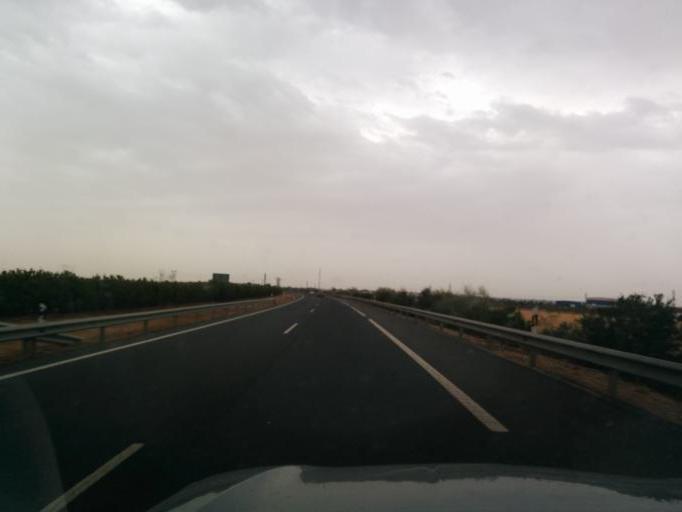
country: ES
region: Andalusia
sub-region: Provincia de Huelva
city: San Juan del Puerto
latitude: 37.3150
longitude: -6.8967
